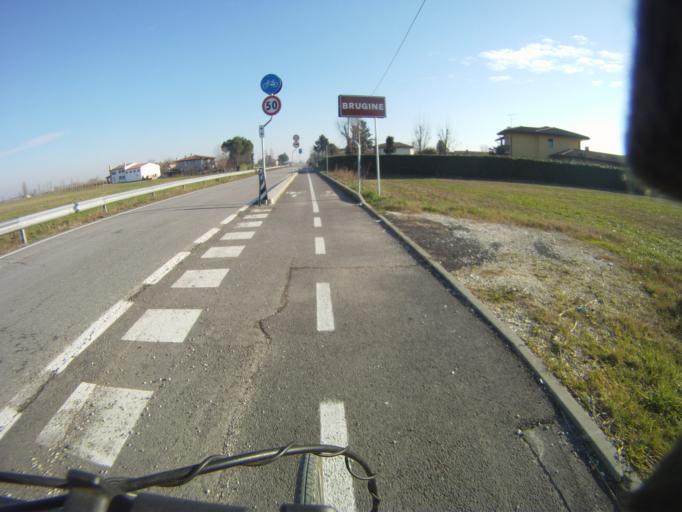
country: IT
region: Veneto
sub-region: Provincia di Padova
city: Brugine
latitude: 45.3123
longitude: 11.9770
